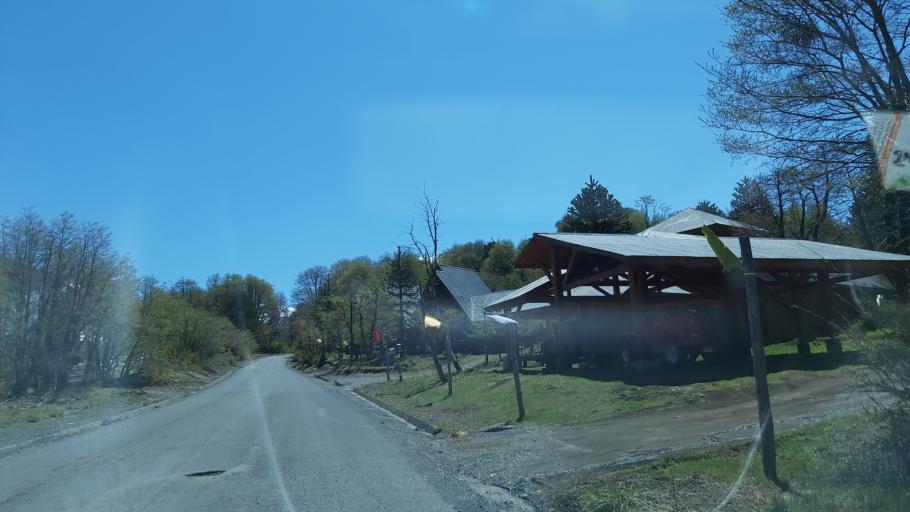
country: CL
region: Araucania
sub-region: Provincia de Cautin
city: Vilcun
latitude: -38.4366
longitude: -71.5321
